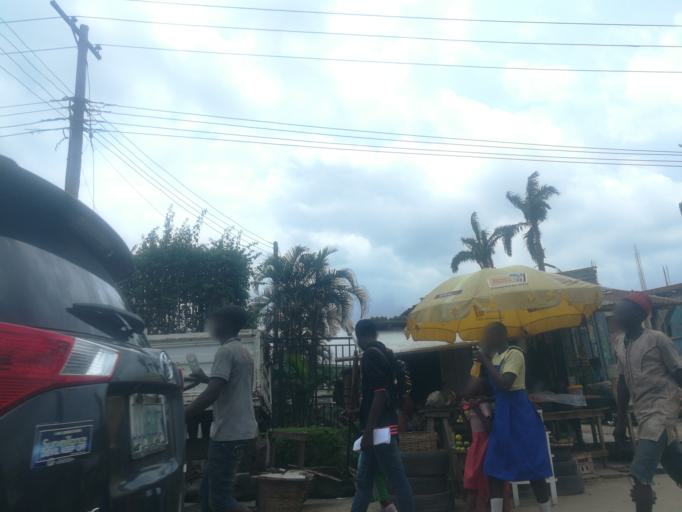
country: NG
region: Lagos
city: Somolu
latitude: 6.5596
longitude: 3.3919
